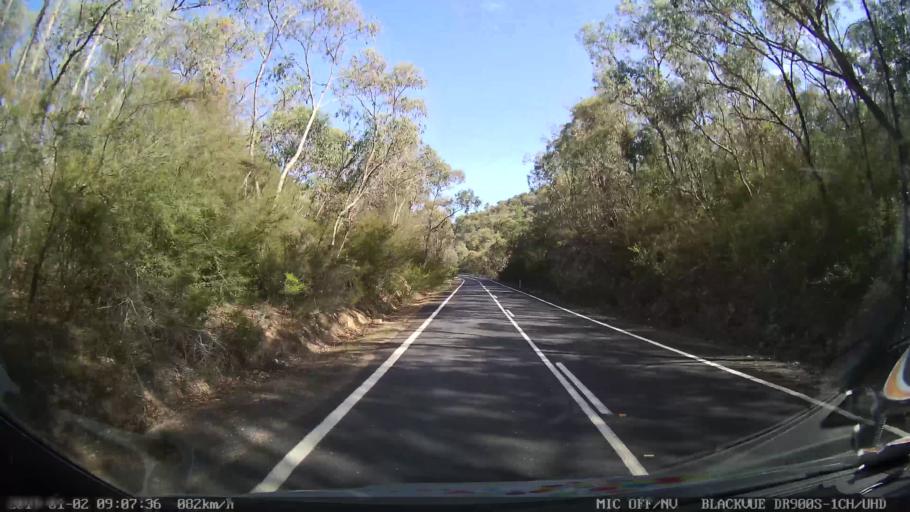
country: AU
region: New South Wales
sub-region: Tumut Shire
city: Tumut
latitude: -35.5393
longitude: 148.2973
